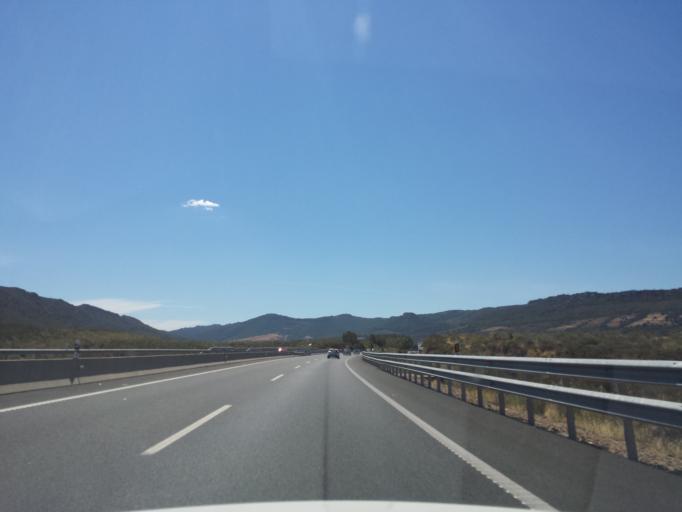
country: ES
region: Extremadura
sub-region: Provincia de Caceres
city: Romangordo
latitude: 39.7327
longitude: -5.7203
